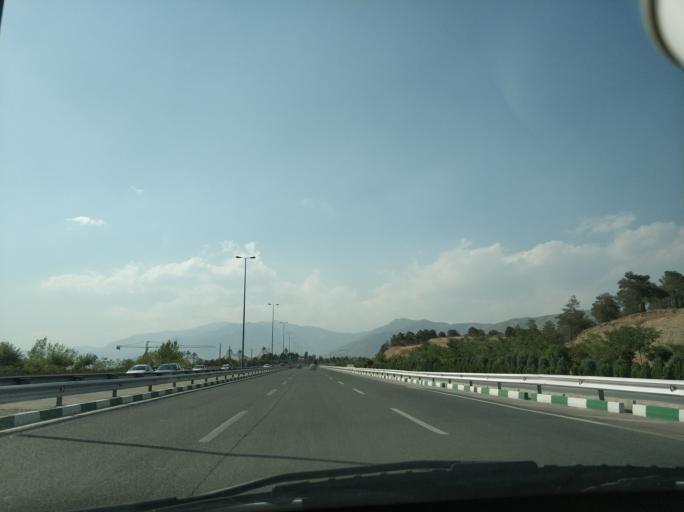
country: IR
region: Tehran
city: Tajrish
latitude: 35.7655
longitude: 51.5375
